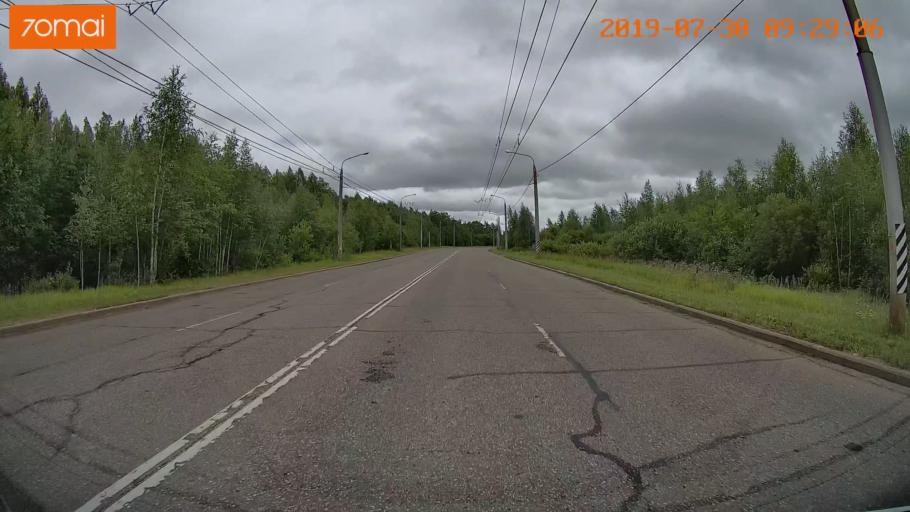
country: RU
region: Ivanovo
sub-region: Gorod Ivanovo
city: Ivanovo
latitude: 56.9471
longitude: 40.9471
